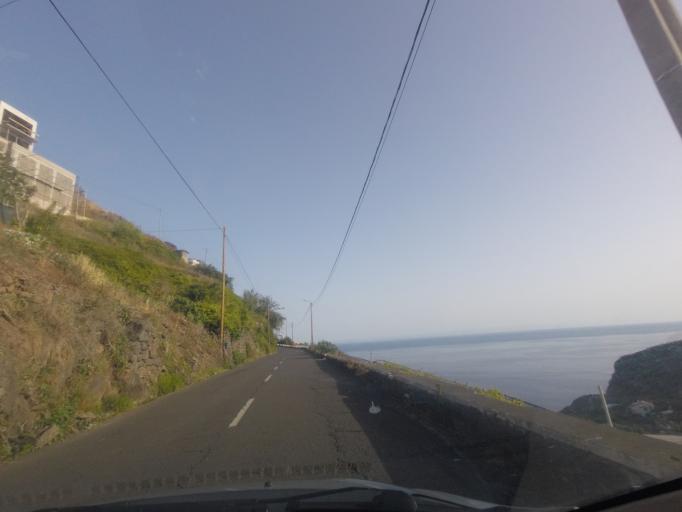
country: PT
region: Madeira
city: Ponta do Sol
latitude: 32.6805
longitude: -17.0727
